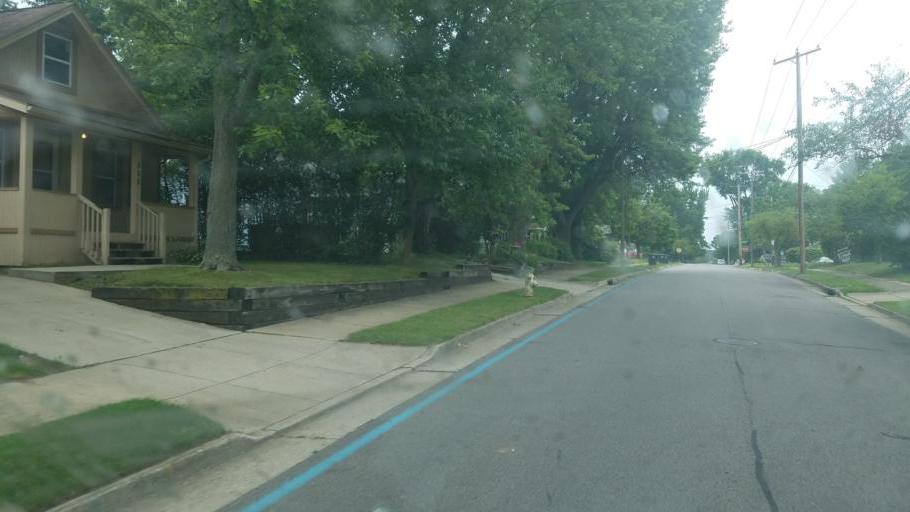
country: US
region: Ohio
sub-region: Summit County
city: Sawyerwood
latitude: 41.0488
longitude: -81.4261
